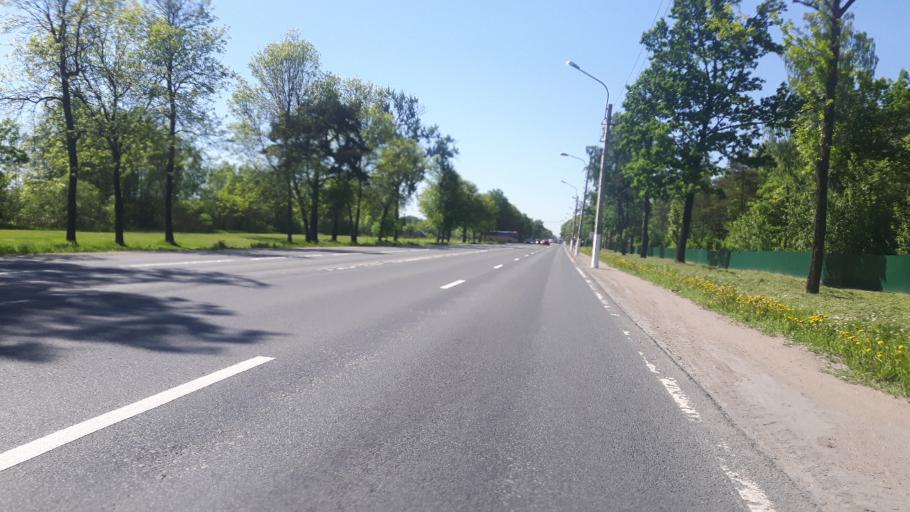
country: RU
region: Leningrad
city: Ol'gino
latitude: 59.8719
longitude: 29.9660
